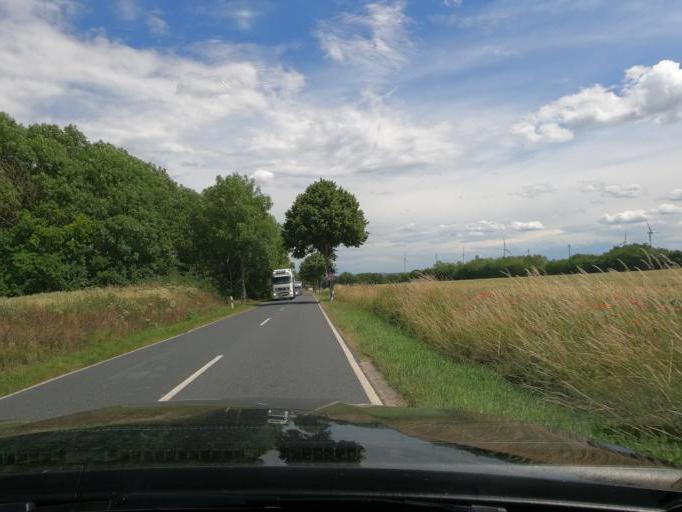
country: DE
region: Lower Saxony
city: Sohlde
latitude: 52.1851
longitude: 10.2629
